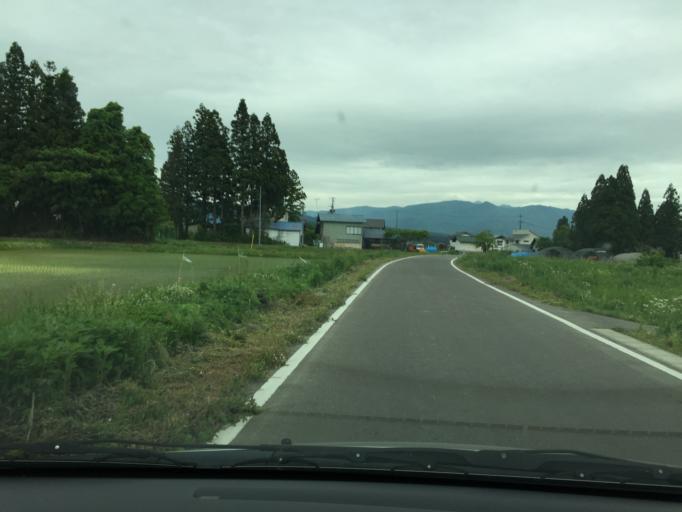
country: JP
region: Fukushima
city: Kitakata
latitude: 37.6848
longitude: 139.8731
